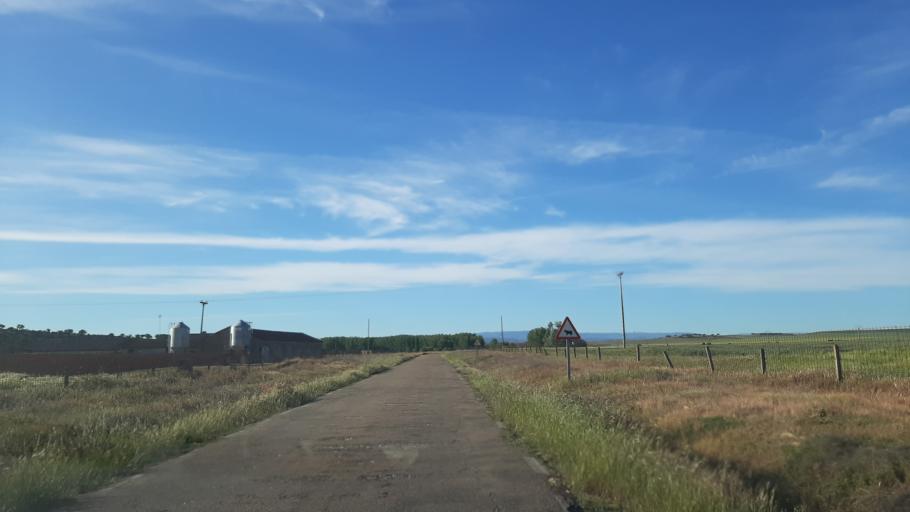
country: ES
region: Castille and Leon
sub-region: Provincia de Salamanca
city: Gajates
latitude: 40.7980
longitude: -5.3738
